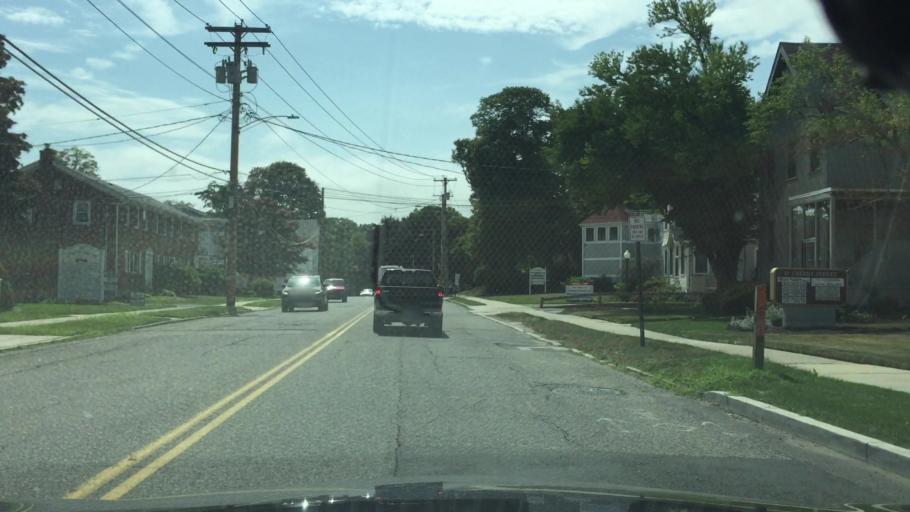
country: US
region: Connecticut
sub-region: New Haven County
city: Milford
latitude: 41.2267
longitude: -73.0548
